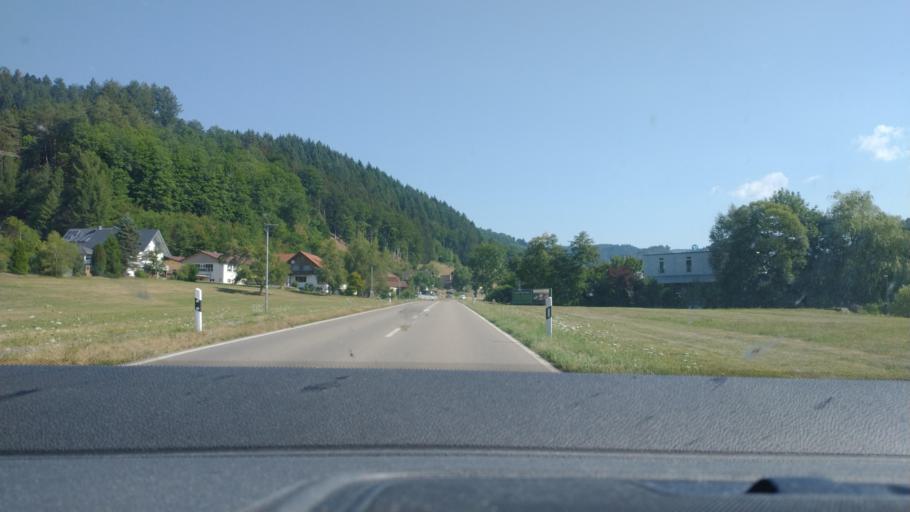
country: DE
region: Baden-Wuerttemberg
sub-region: Freiburg Region
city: Nordrach
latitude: 48.3880
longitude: 8.0707
